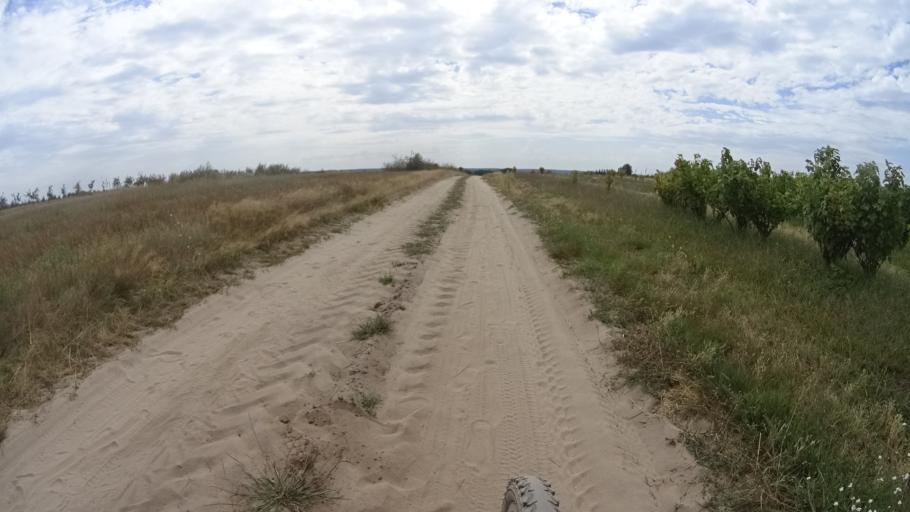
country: PL
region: Masovian Voivodeship
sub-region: Powiat bialobrzeski
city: Wysmierzyce
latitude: 51.6558
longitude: 20.7956
